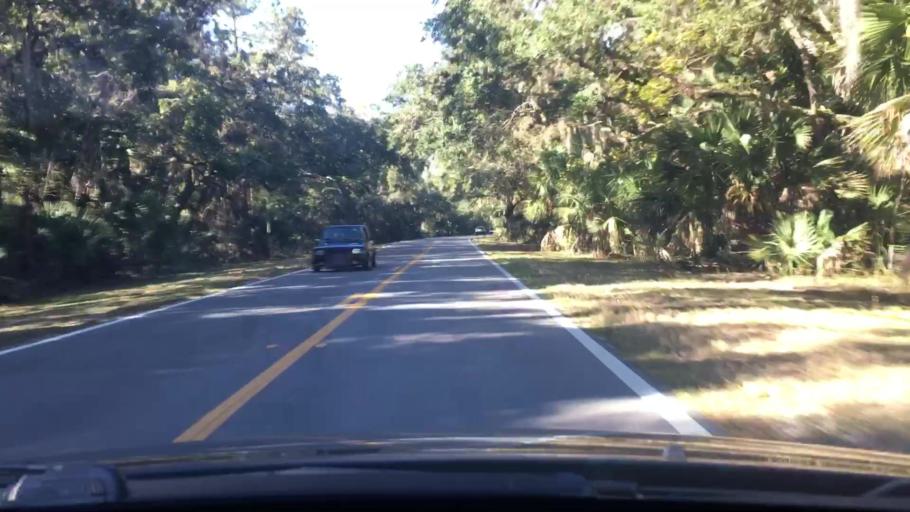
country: US
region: Florida
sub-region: Volusia County
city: Ormond-by-the-Sea
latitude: 29.3629
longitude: -81.1230
